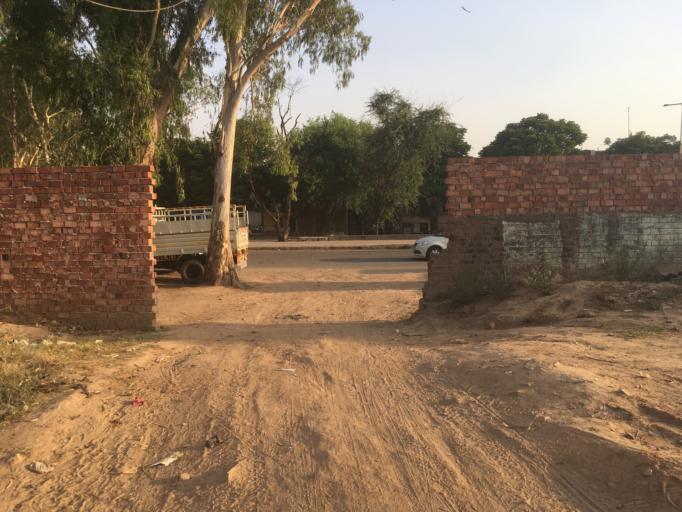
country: IN
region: Chandigarh
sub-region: Chandigarh
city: Chandigarh
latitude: 30.7017
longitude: 76.8320
